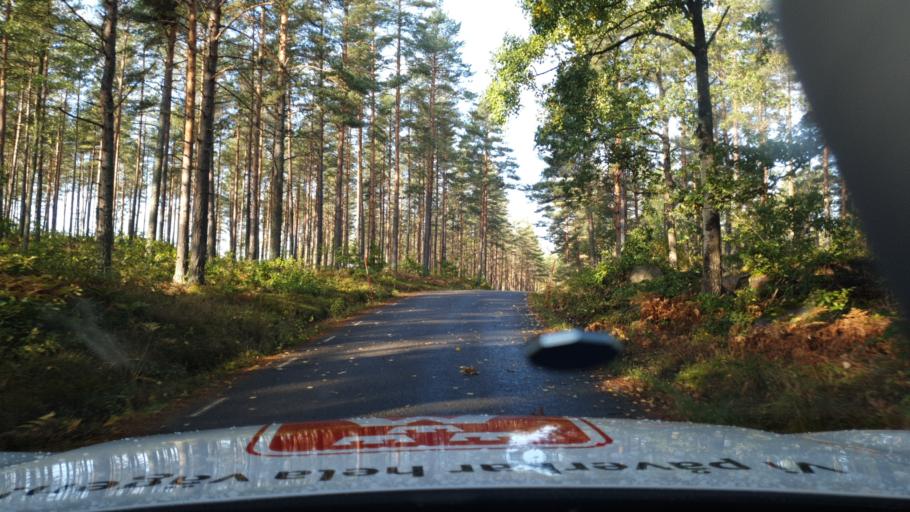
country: SE
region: Kalmar
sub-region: Vasterviks Kommun
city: Forserum
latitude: 57.9937
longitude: 16.5600
